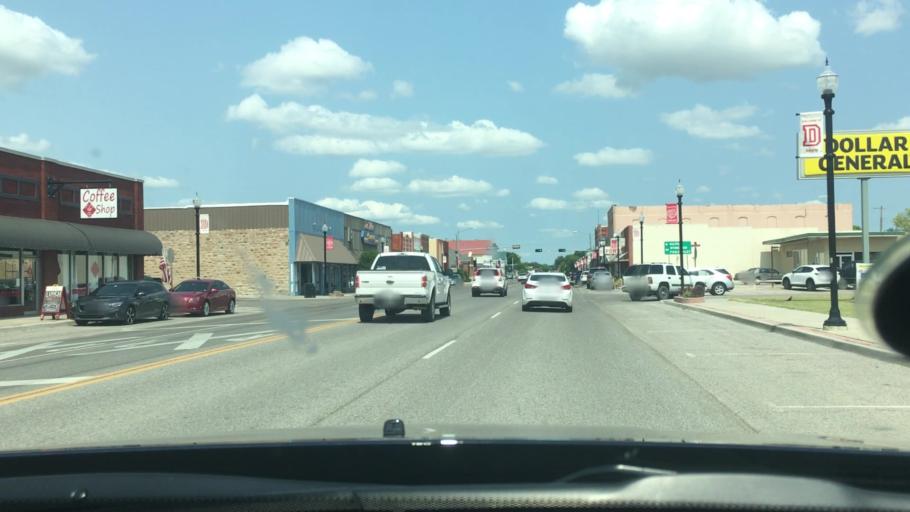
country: US
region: Oklahoma
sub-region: Murray County
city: Davis
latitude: 34.5039
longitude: -97.1213
